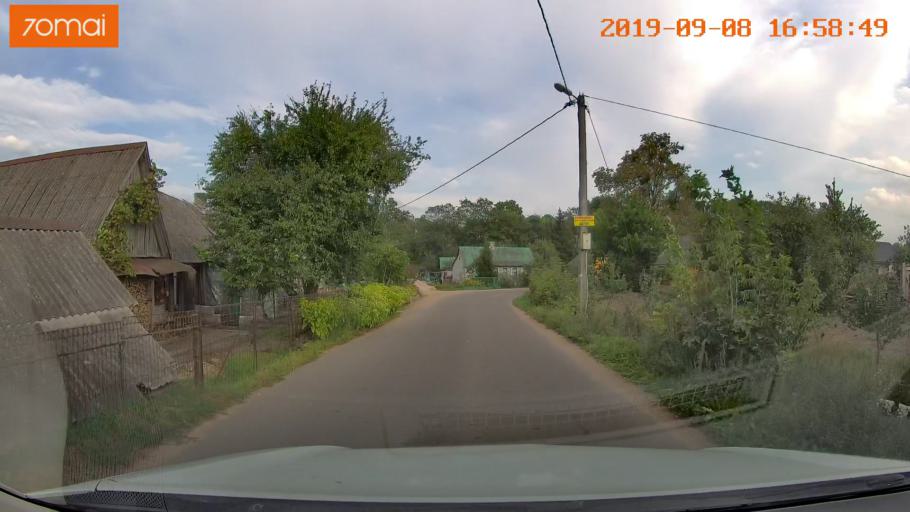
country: BY
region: Grodnenskaya
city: Hrodna
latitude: 53.7250
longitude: 23.9314
